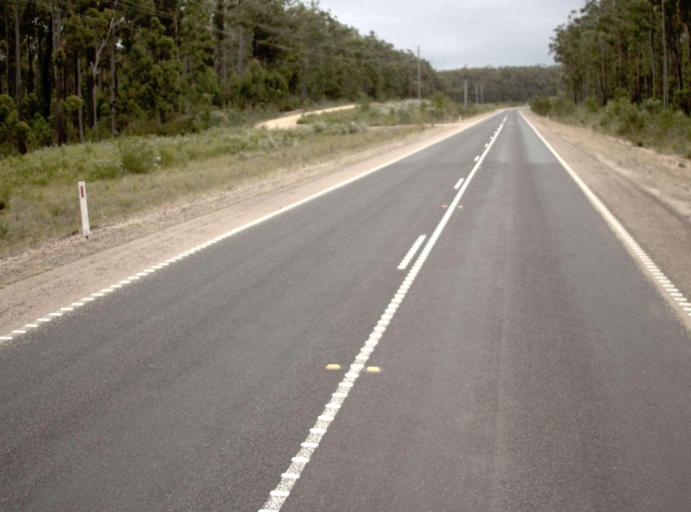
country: AU
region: Victoria
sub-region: East Gippsland
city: Lakes Entrance
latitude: -37.7046
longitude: 148.0560
